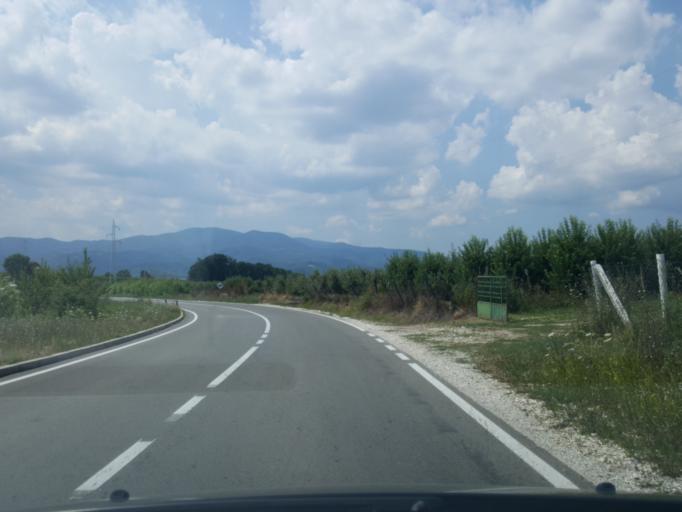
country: RS
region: Central Serbia
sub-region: Sumadijski Okrug
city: Topola
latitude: 44.2187
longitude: 20.6198
